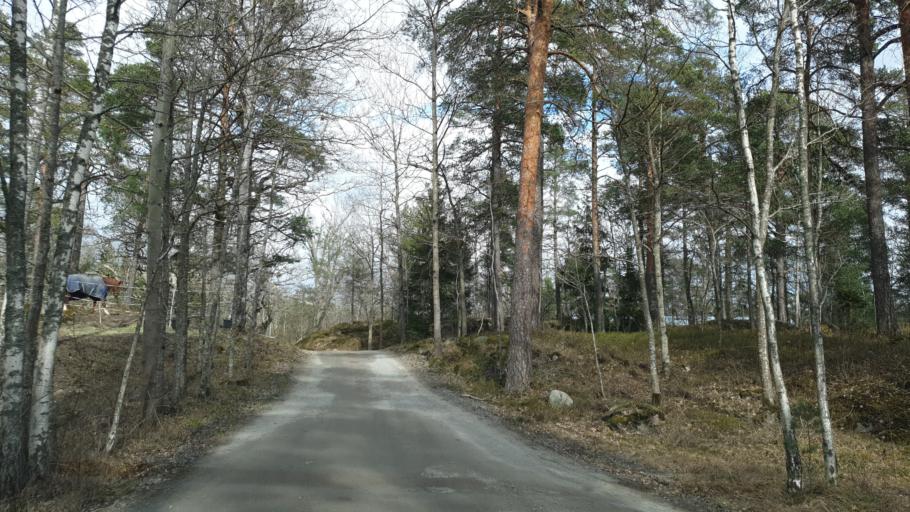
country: SE
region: Stockholm
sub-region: Nacka Kommun
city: Saltsjobaden
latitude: 59.3225
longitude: 18.3356
